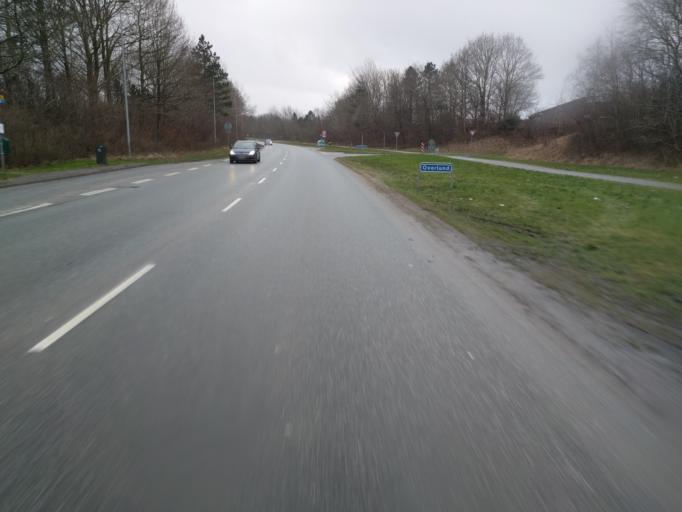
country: DK
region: Central Jutland
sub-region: Viborg Kommune
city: Viborg
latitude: 56.4583
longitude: 9.4446
